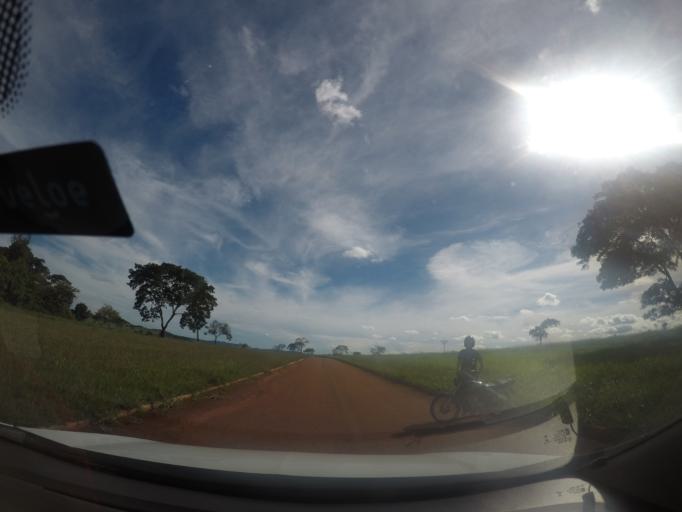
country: BR
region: Goias
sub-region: Inhumas
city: Inhumas
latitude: -16.4071
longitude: -49.4712
